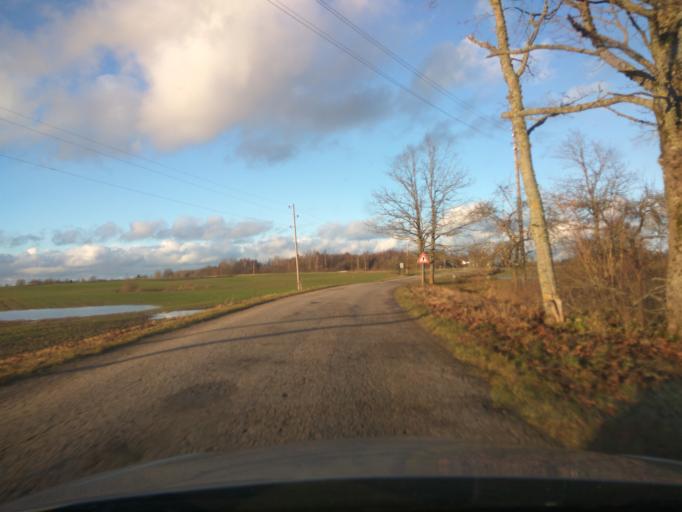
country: LV
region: Aizpute
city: Aizpute
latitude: 56.7707
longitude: 21.7845
